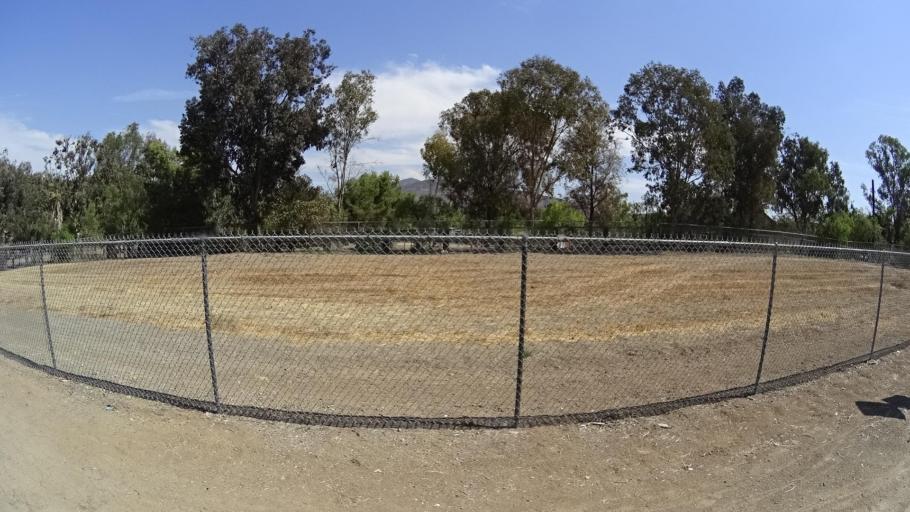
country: US
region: California
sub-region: San Diego County
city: La Presa
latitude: 32.6759
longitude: -116.9986
